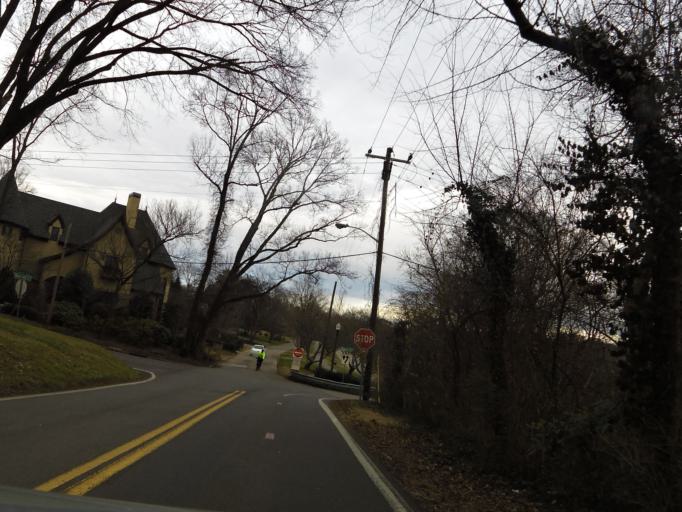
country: US
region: Tennessee
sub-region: Knox County
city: Knoxville
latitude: 35.9316
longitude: -83.9757
